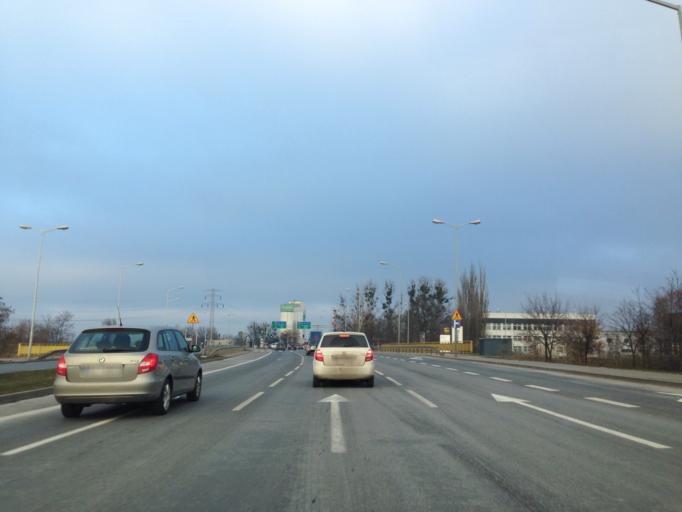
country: PL
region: Greater Poland Voivodeship
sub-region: Poznan
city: Poznan
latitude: 52.4248
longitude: 16.9657
